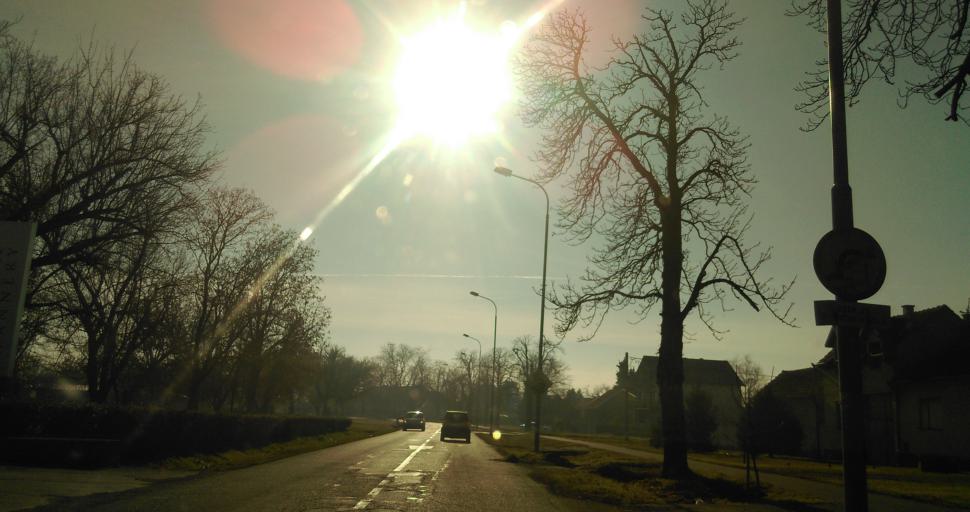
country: RS
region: Autonomna Pokrajina Vojvodina
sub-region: Sremski Okrug
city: Ruma
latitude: 44.9928
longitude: 19.8233
